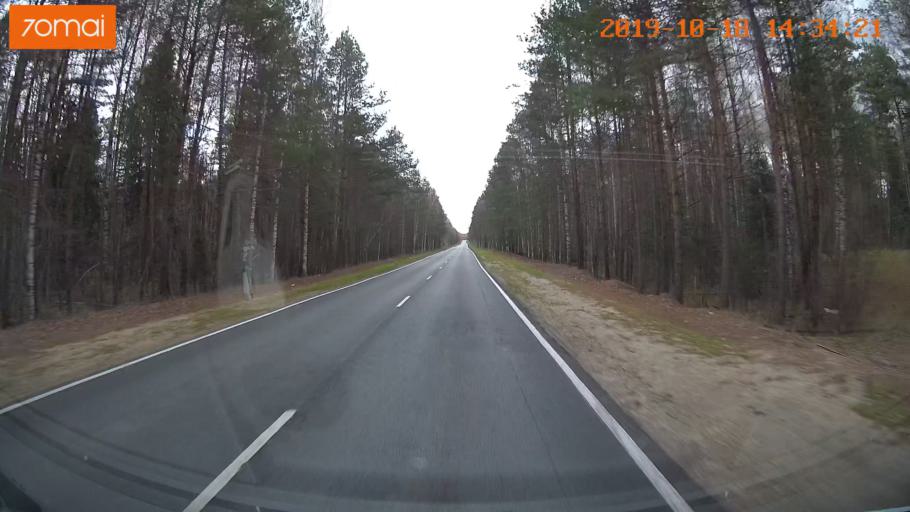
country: RU
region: Vladimir
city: Velikodvorskiy
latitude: 55.2113
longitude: 40.6146
